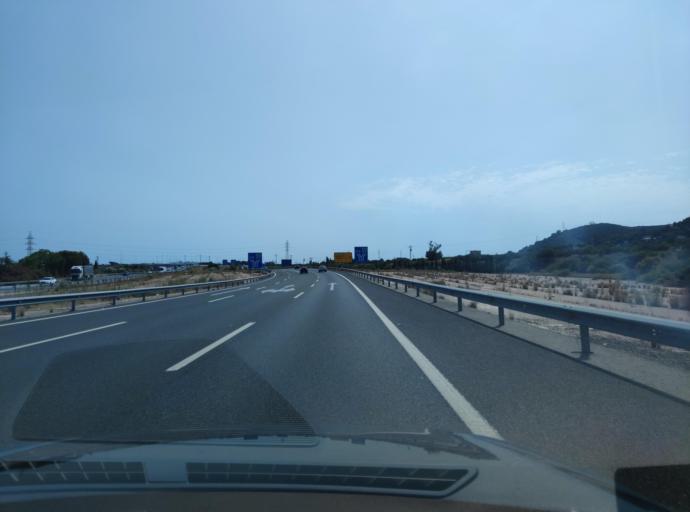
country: ES
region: Valencia
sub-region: Provincia de Valencia
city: Pucol
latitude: 39.6394
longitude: -0.3020
